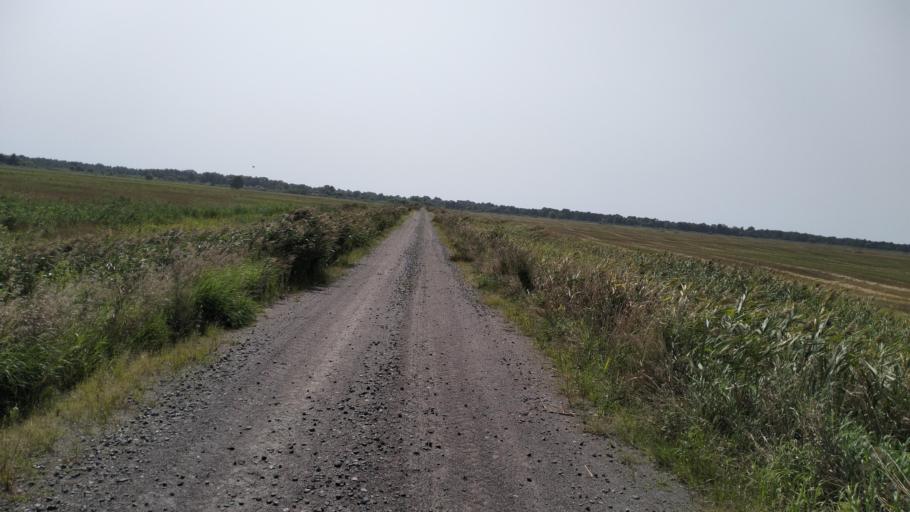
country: BY
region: Brest
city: Davyd-Haradok
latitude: 51.9766
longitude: 27.1745
